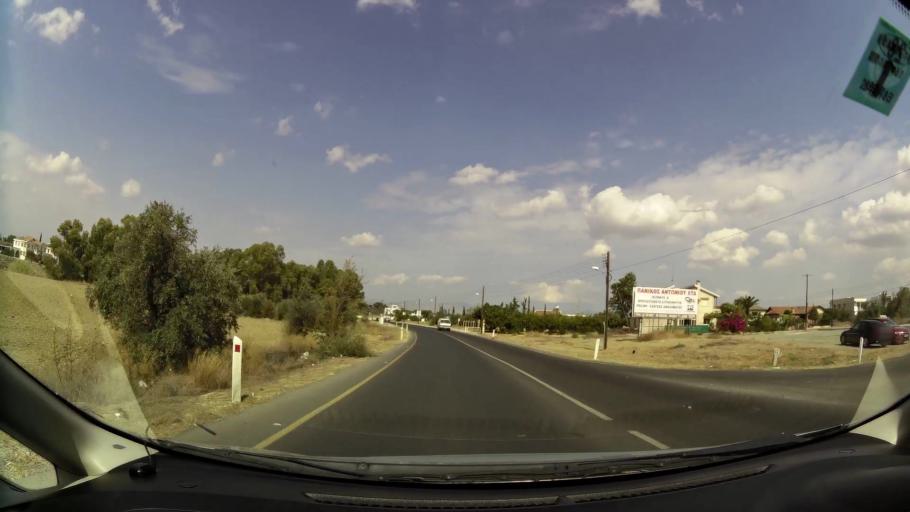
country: CY
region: Lefkosia
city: Tseri
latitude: 35.0860
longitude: 33.3291
